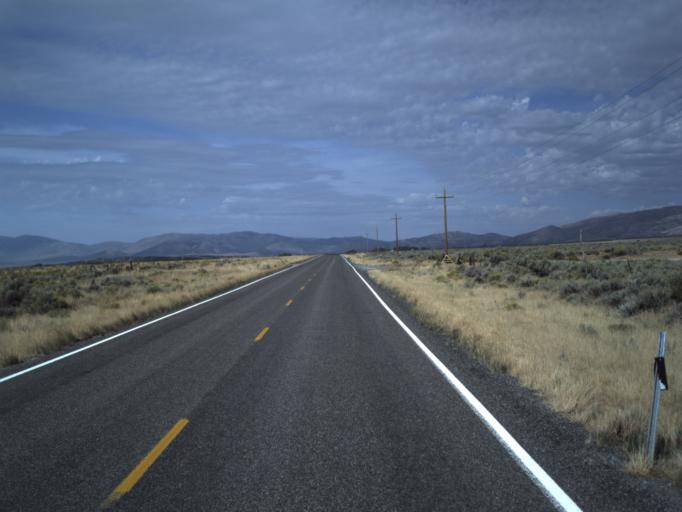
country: US
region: Idaho
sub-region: Cassia County
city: Burley
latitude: 41.8166
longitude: -113.3639
